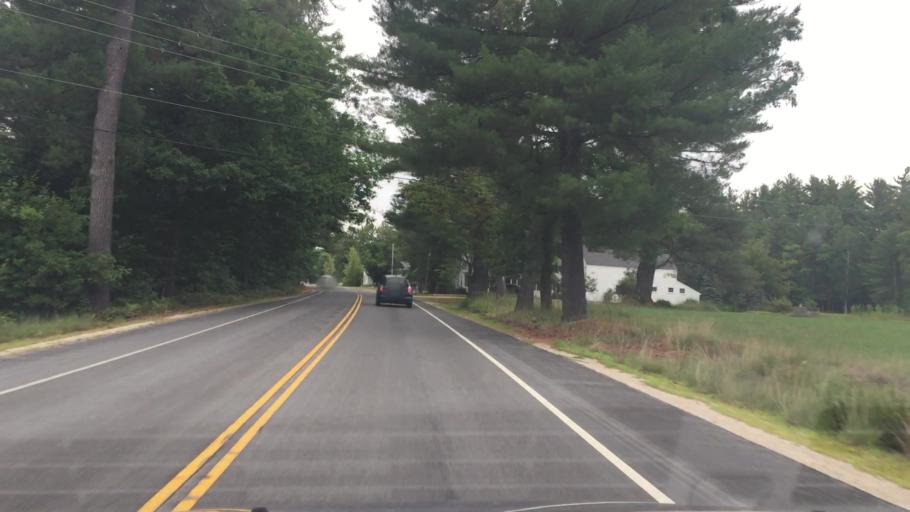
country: US
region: New Hampshire
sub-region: Carroll County
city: Tamworth
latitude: 43.8501
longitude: -71.2635
